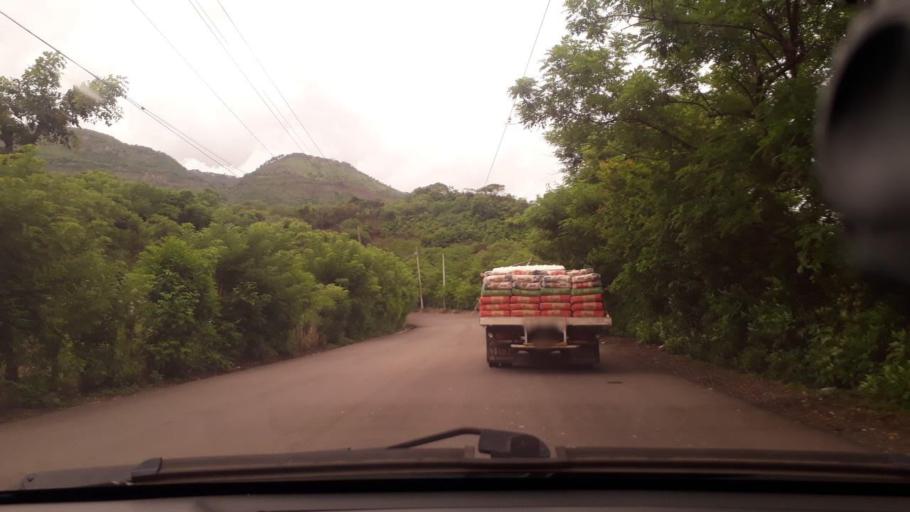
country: GT
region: Chiquimula
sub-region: Municipio de San Juan Ermita
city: San Juan Ermita
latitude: 14.7354
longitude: -89.4719
